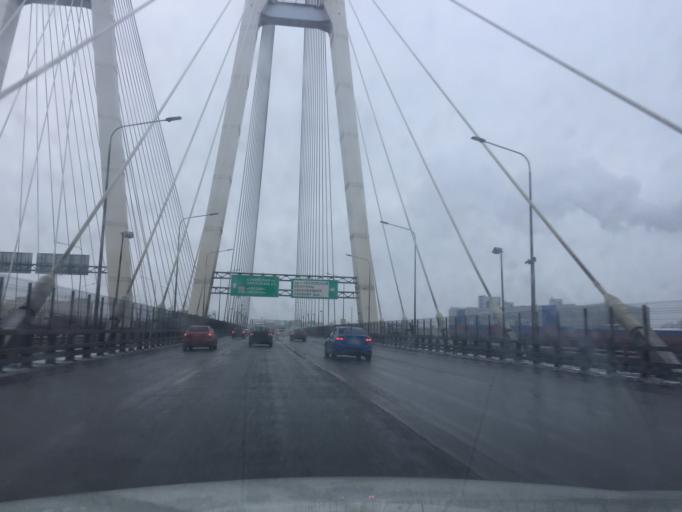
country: RU
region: Leningrad
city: Rybatskoye
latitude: 59.8535
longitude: 30.4909
